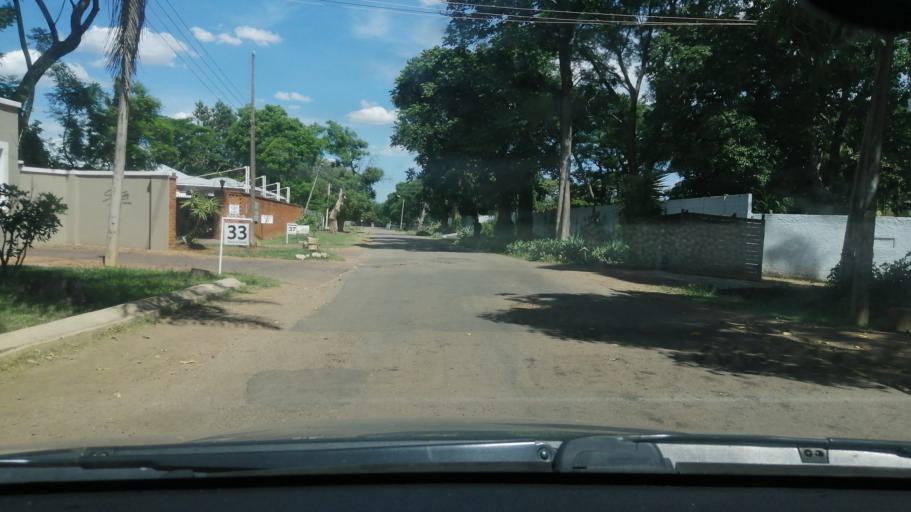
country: ZW
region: Harare
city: Harare
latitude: -17.8124
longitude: 31.0799
